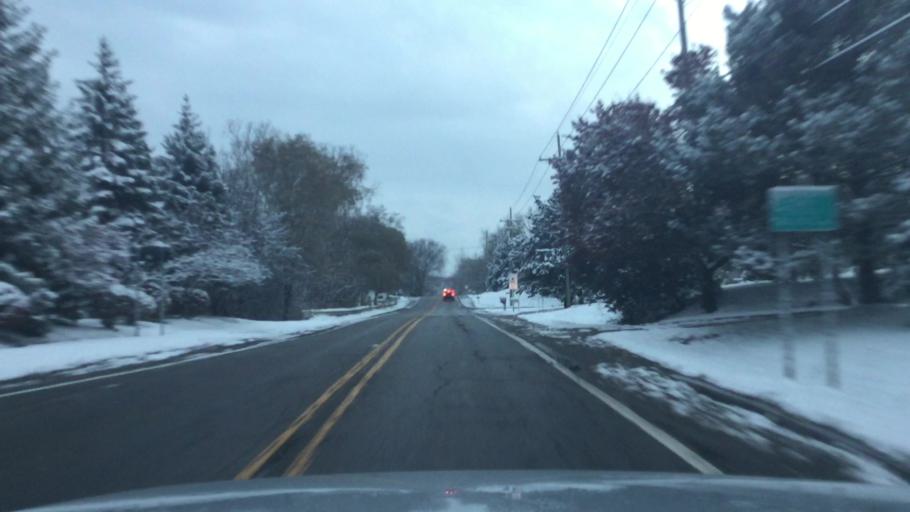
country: US
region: Michigan
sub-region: Oakland County
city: West Bloomfield Township
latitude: 42.6056
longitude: -83.3982
